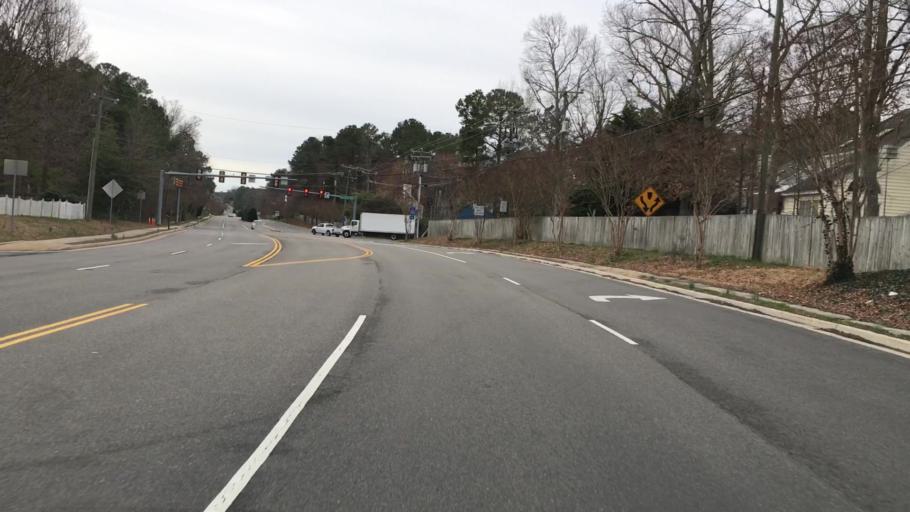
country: US
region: Virginia
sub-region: Henrico County
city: Short Pump
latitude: 37.6639
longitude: -77.5622
